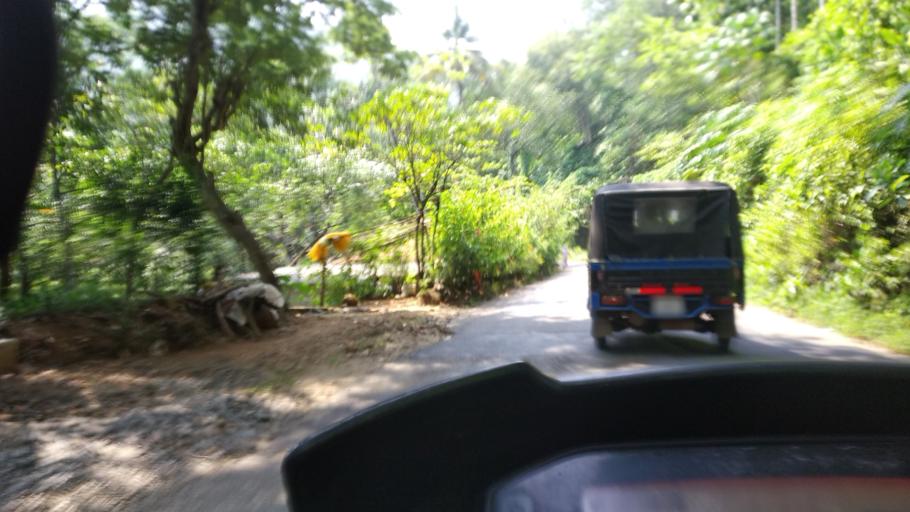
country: IN
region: Kerala
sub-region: Kottayam
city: Erattupetta
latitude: 9.6877
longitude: 76.8333
